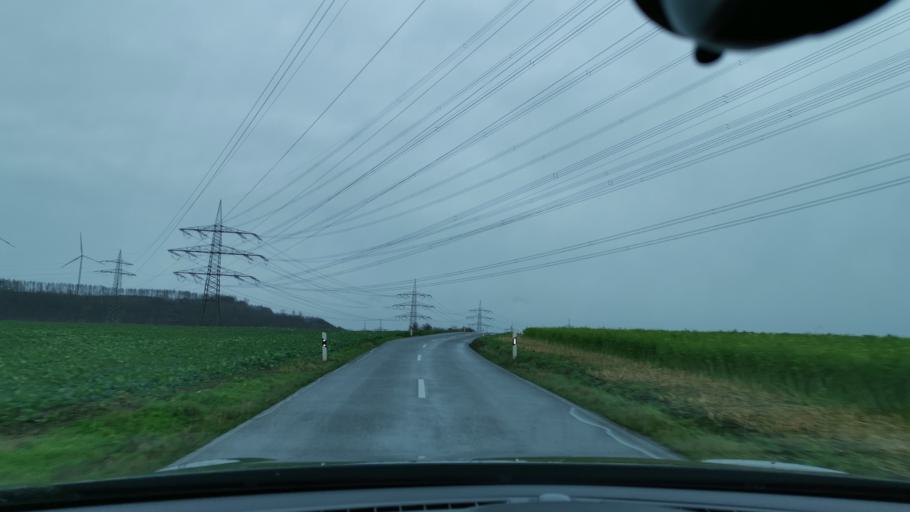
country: DE
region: North Rhine-Westphalia
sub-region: Regierungsbezirk Dusseldorf
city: Grevenbroich
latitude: 51.0471
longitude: 6.6086
